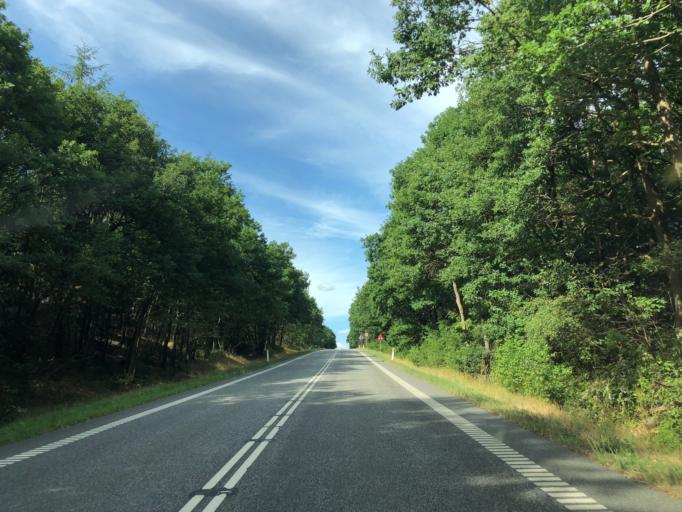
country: DK
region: Central Jutland
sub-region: Ikast-Brande Kommune
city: Bording Kirkeby
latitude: 56.1382
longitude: 9.3932
